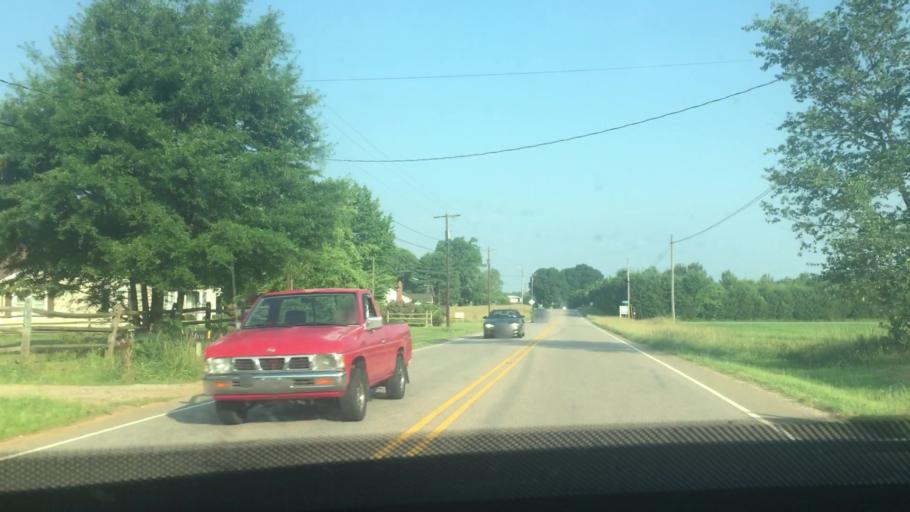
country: US
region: North Carolina
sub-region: Rowan County
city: Enochville
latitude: 35.5806
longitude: -80.7181
